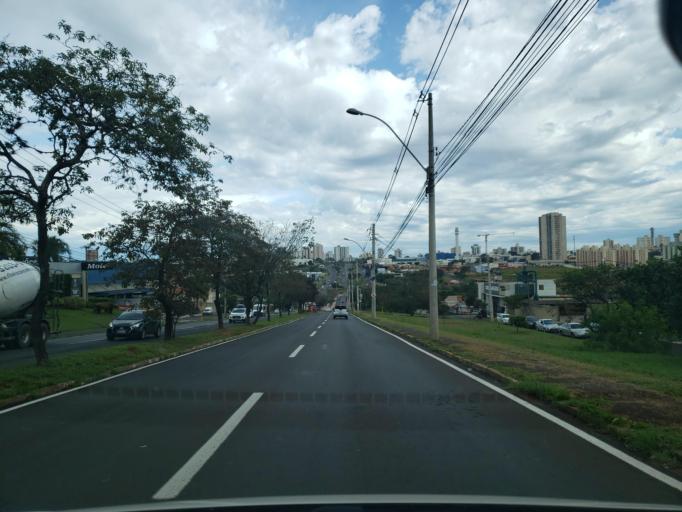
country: BR
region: Sao Paulo
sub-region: Bauru
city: Bauru
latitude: -22.3362
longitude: -49.0356
